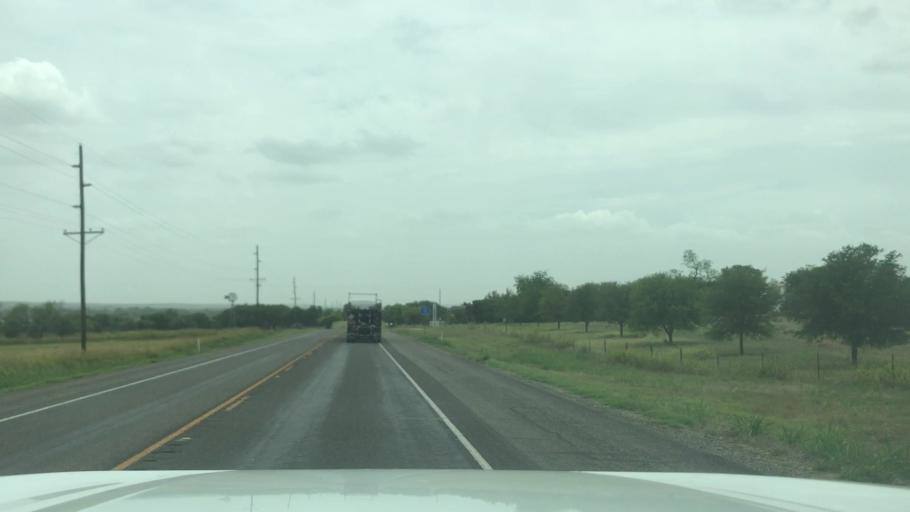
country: US
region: Texas
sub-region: Bosque County
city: Clifton
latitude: 31.7554
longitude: -97.5597
